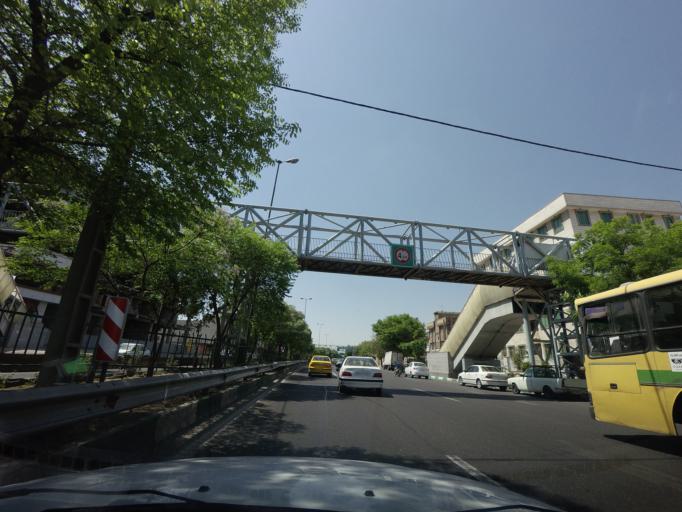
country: IR
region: Tehran
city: Tehran
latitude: 35.6409
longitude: 51.3646
